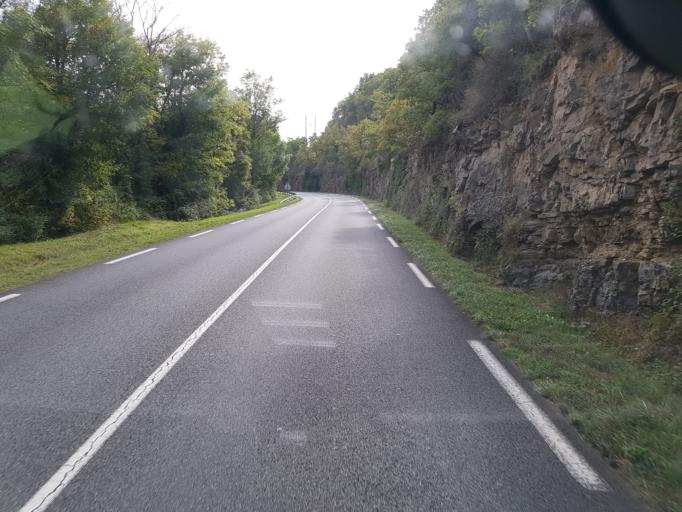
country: FR
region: Midi-Pyrenees
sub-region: Departement de l'Aveyron
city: Saint-Georges-de-Luzencon
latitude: 44.0291
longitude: 2.9648
